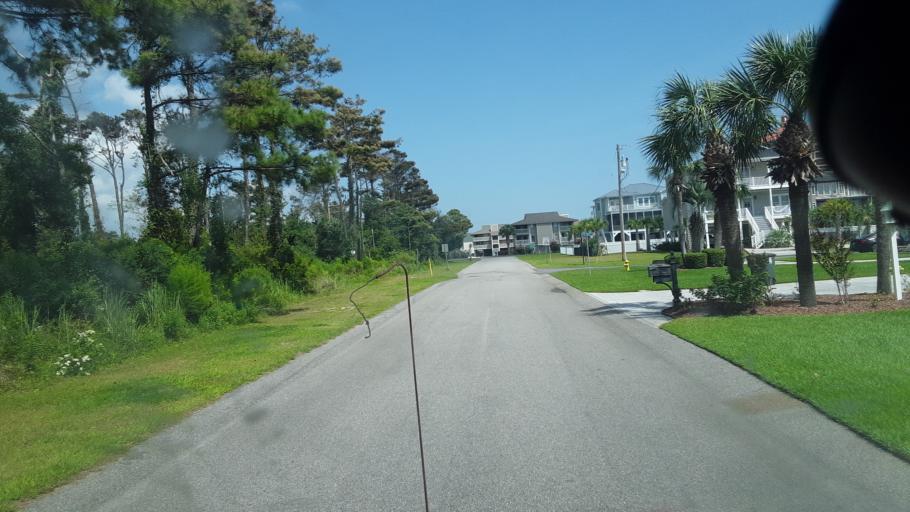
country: US
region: South Carolina
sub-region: Horry County
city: North Myrtle Beach
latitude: 33.8271
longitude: -78.6541
